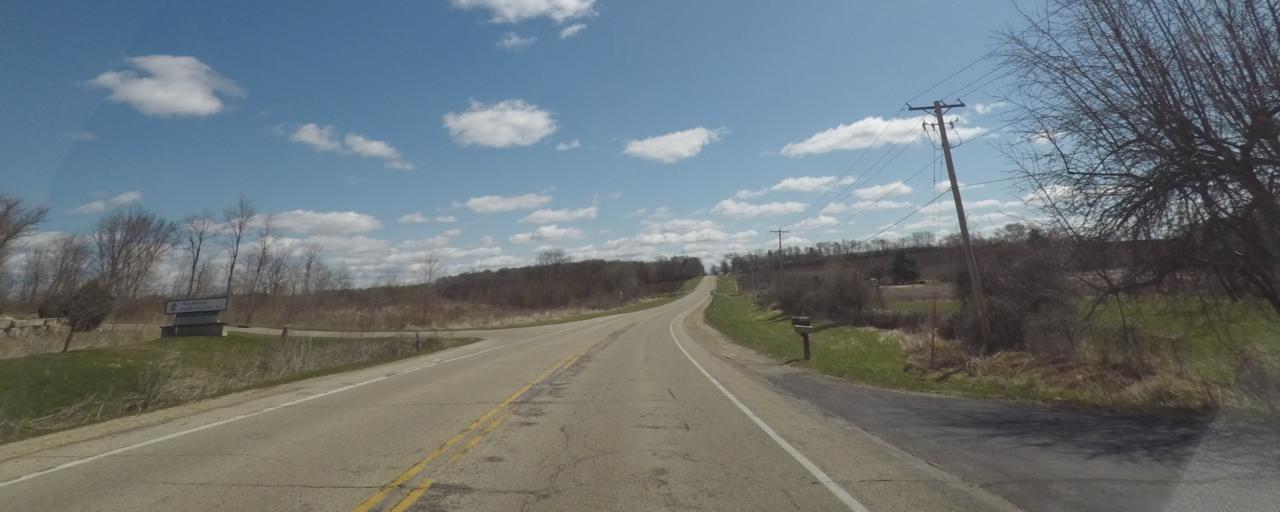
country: US
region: Wisconsin
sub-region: Dane County
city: Cottage Grove
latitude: 43.0897
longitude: -89.1937
